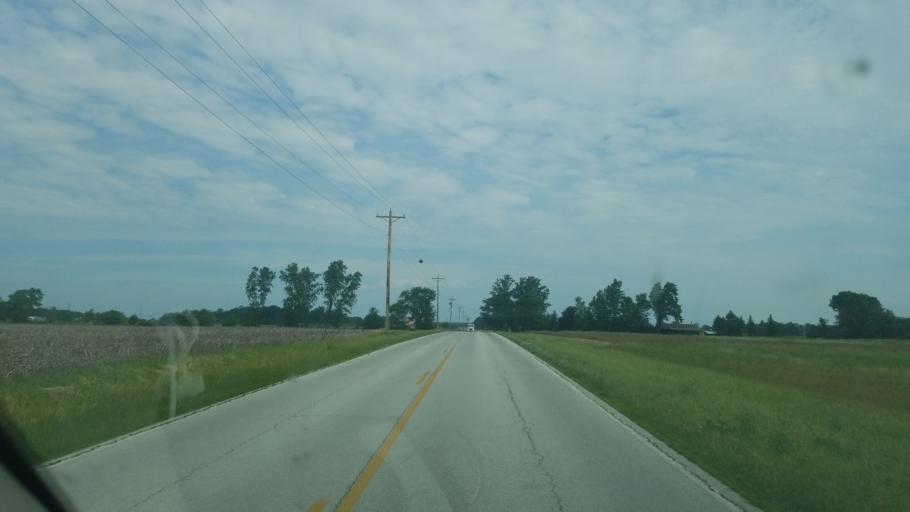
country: US
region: Ohio
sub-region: Seneca County
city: Fostoria
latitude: 41.1208
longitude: -83.4787
